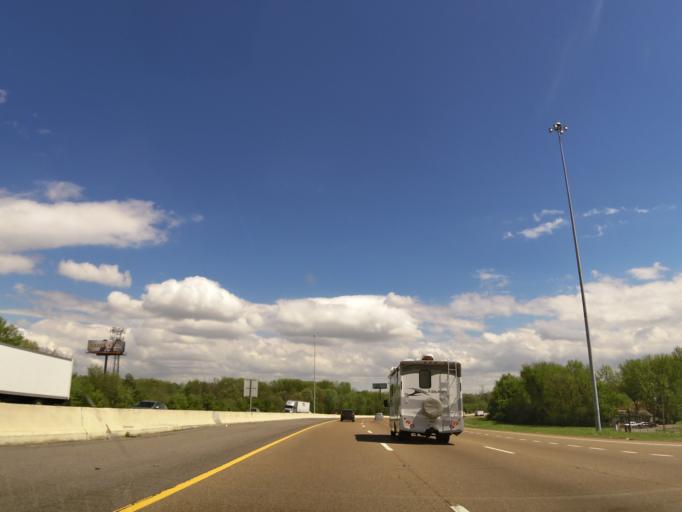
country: US
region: Tennessee
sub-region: Shelby County
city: Bartlett
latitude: 35.1925
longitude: -89.9242
